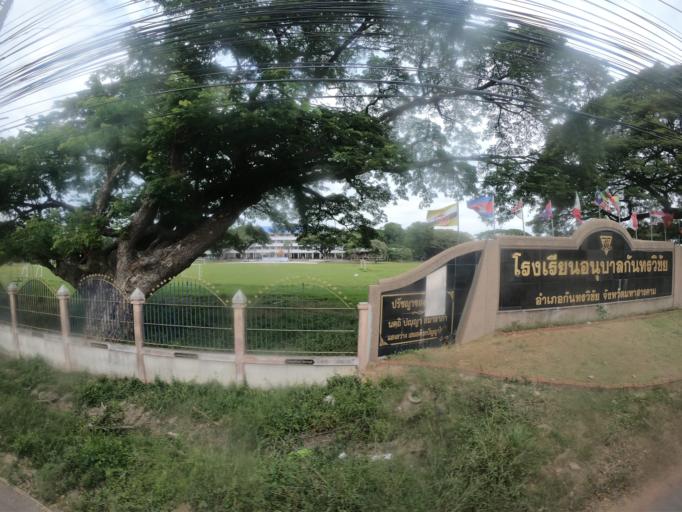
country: TH
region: Maha Sarakham
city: Kantharawichai
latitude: 16.3259
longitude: 103.2956
